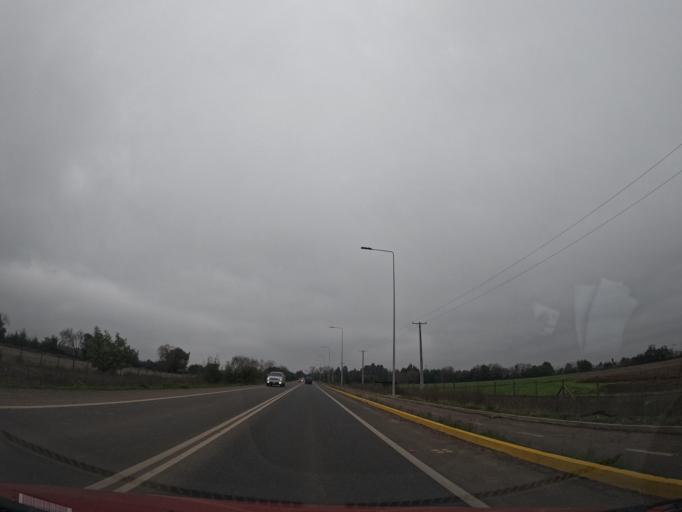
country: CL
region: Maule
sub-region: Provincia de Talca
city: San Clemente
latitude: -35.5406
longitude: -71.4733
